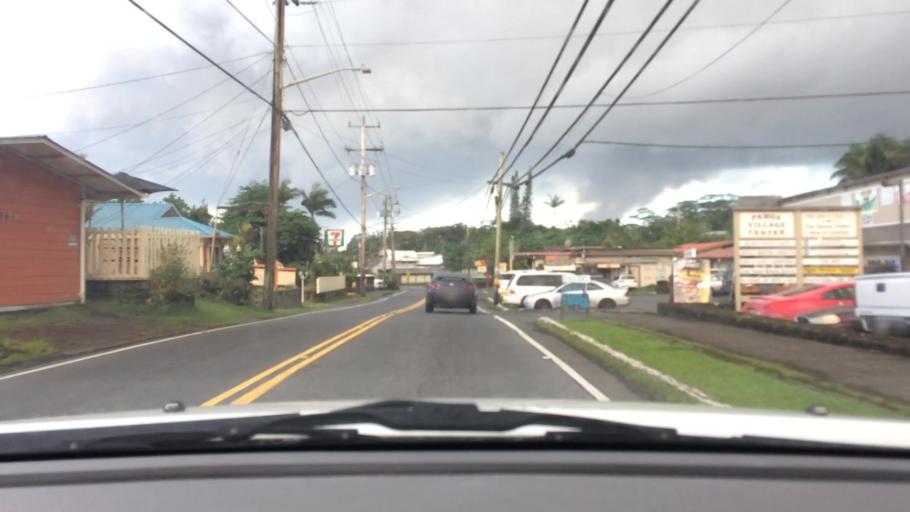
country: US
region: Hawaii
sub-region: Hawaii County
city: Hawaiian Paradise Park
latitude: 19.4951
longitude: -154.9489
